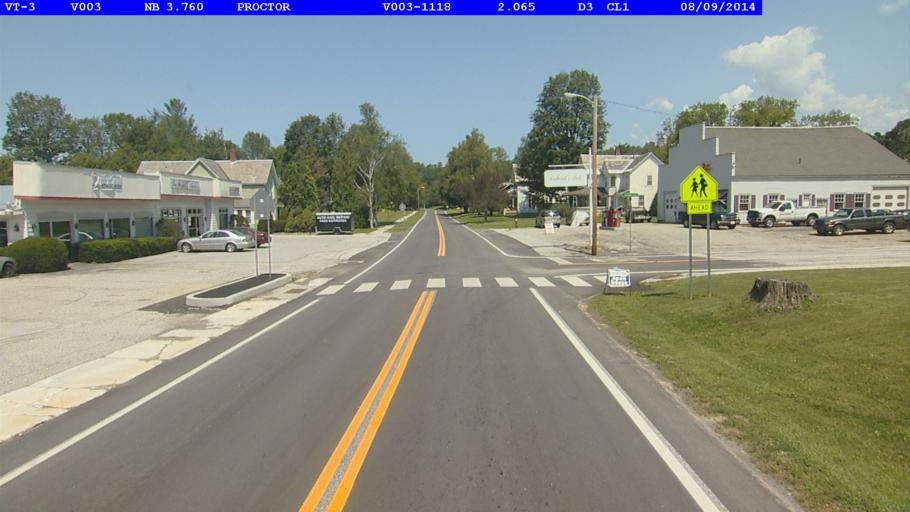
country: US
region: Vermont
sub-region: Rutland County
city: West Rutland
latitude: 43.6534
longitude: -73.0314
